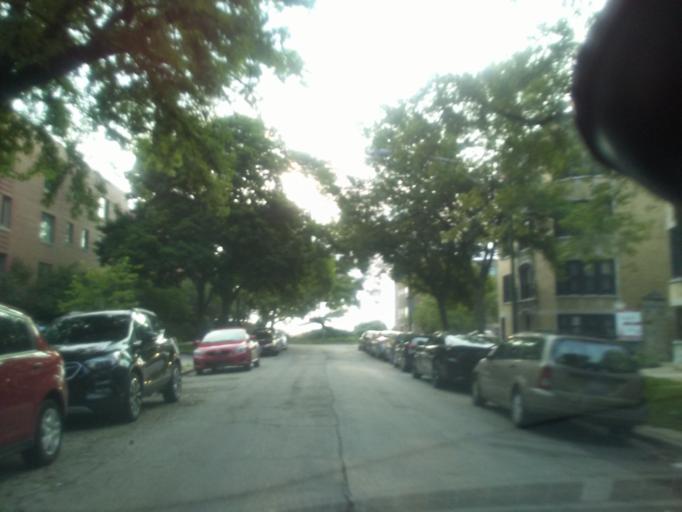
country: US
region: Illinois
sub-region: Cook County
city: Evanston
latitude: 42.0139
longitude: -87.6633
